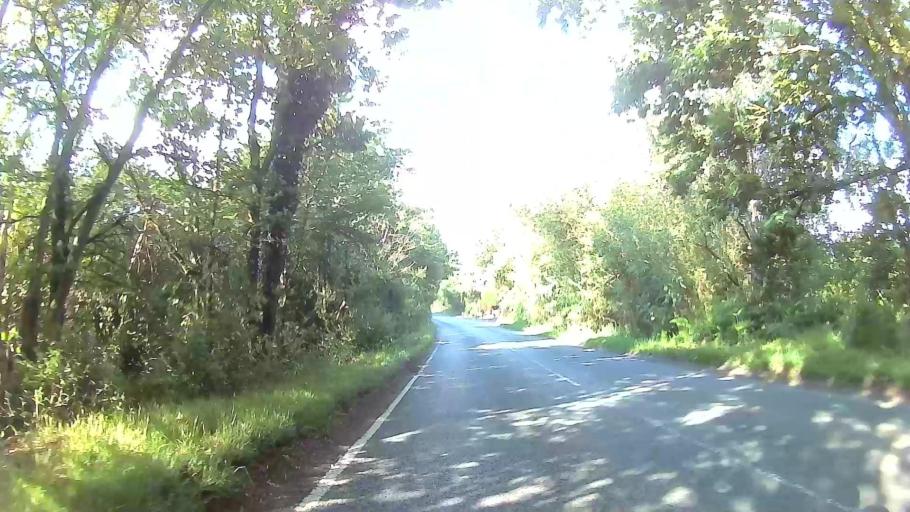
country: GB
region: England
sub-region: Essex
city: Kelvedon Hatch
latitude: 51.6675
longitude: 0.2830
